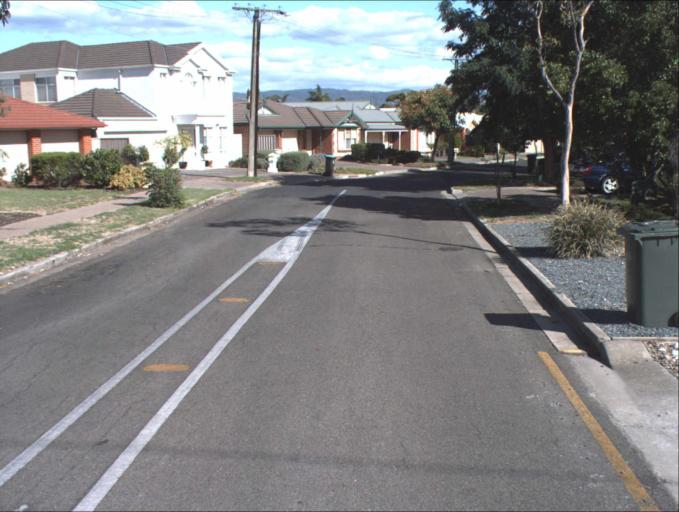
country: AU
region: South Australia
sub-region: Port Adelaide Enfield
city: Gilles Plains
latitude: -34.8622
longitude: 138.6438
